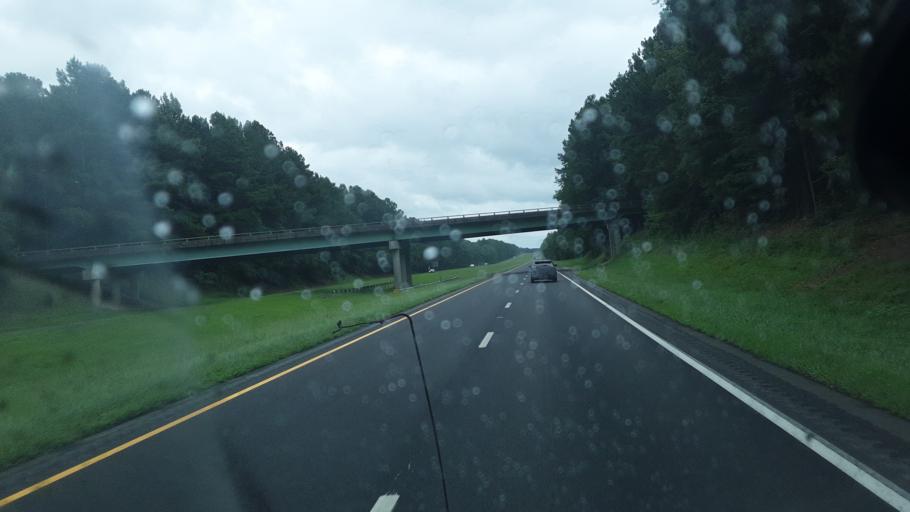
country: US
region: North Carolina
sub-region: Montgomery County
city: Biscoe
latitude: 35.3343
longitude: -79.7507
